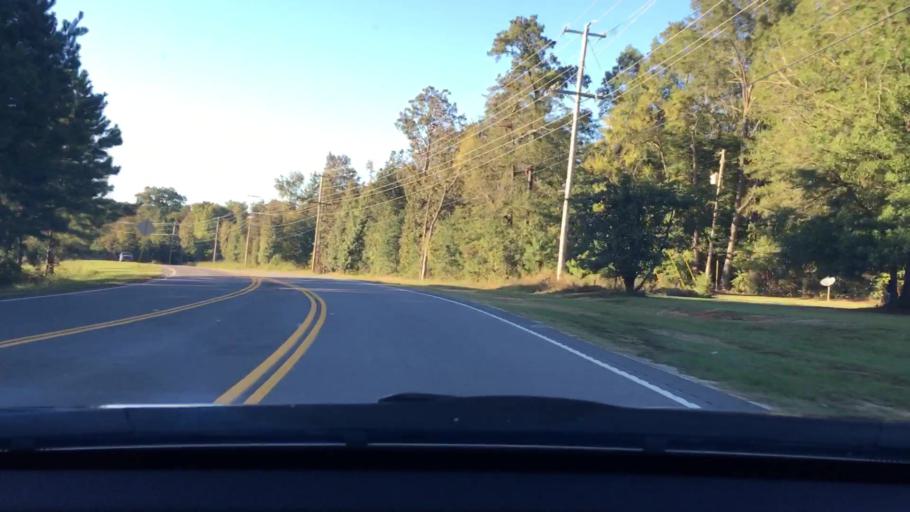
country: US
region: South Carolina
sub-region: Lexington County
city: Irmo
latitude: 34.0992
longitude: -81.1675
